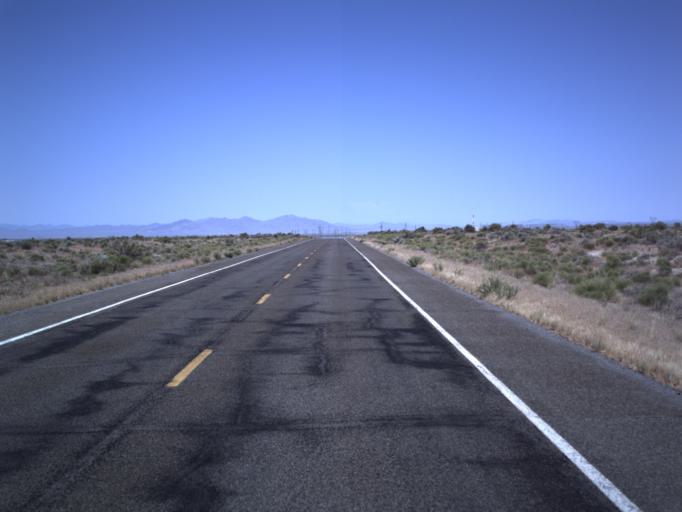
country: US
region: Utah
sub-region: Millard County
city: Delta
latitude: 39.4887
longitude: -112.5491
